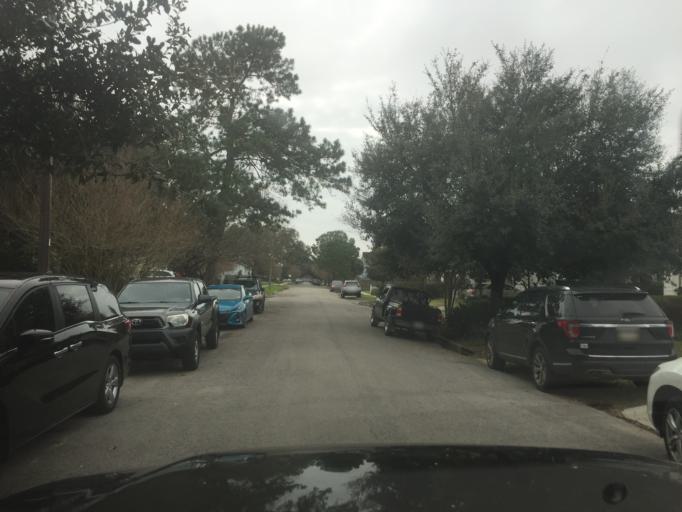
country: US
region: Louisiana
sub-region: Jefferson Parish
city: Metairie
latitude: 30.0002
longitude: -90.1053
